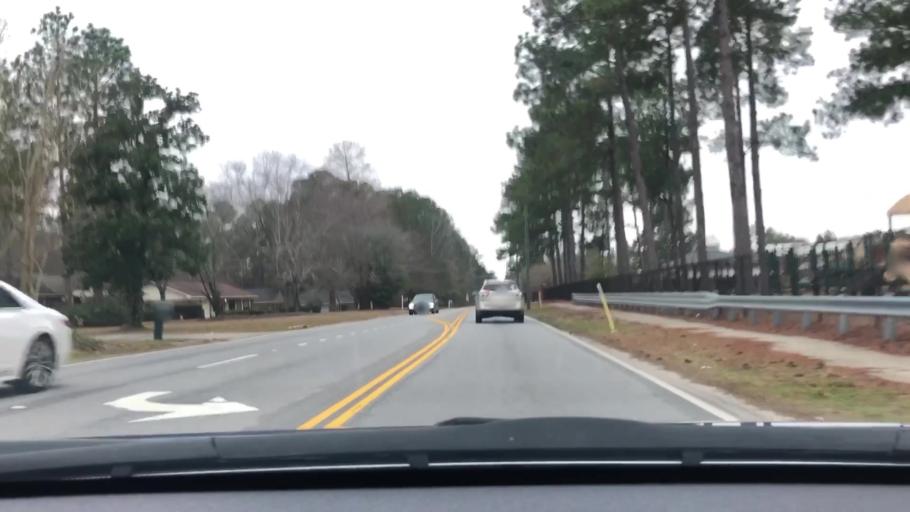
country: US
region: South Carolina
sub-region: Sumter County
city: Cane Savannah
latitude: 33.9346
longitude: -80.4048
